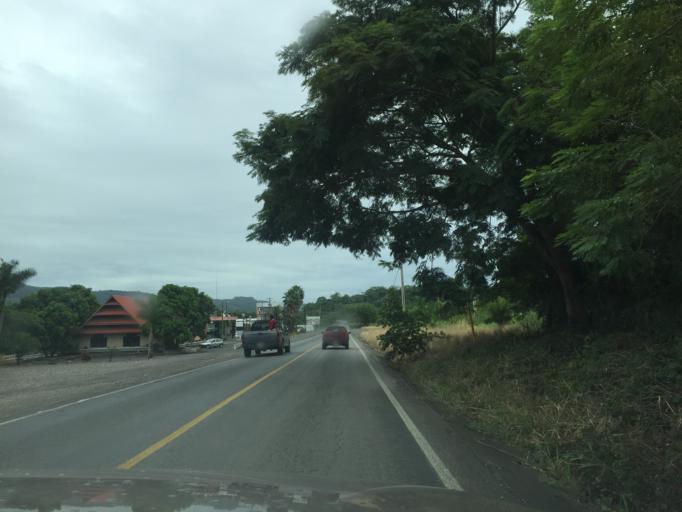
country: MX
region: Veracruz
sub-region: Papantla
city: El Chote
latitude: 20.4393
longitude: -97.3966
